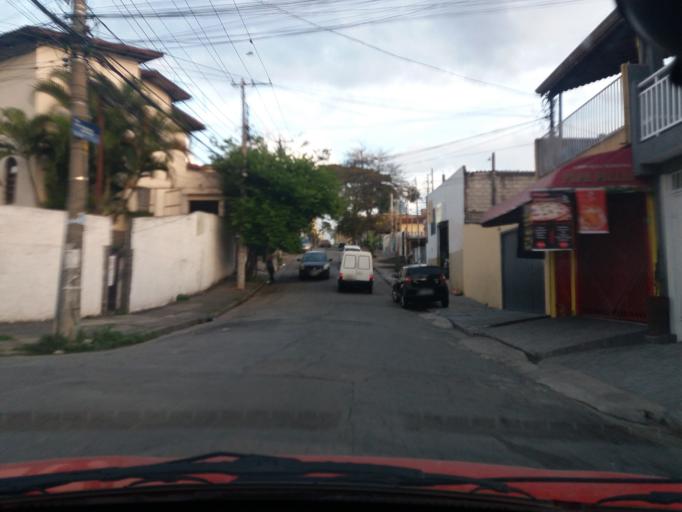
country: BR
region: Sao Paulo
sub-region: Taboao Da Serra
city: Taboao da Serra
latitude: -23.6033
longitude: -46.7421
